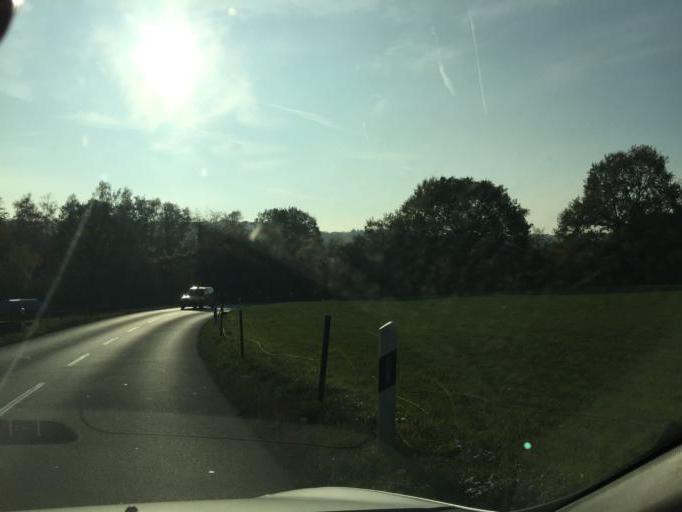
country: LU
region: Luxembourg
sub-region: Canton de Luxembourg
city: Contern
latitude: 49.5690
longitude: 6.2173
